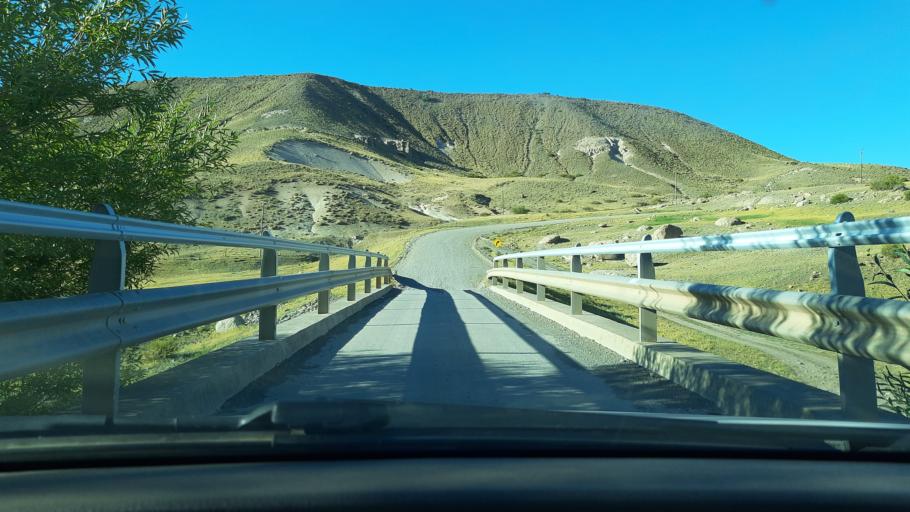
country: AR
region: Neuquen
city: Las Ovejas
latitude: -36.8233
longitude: -70.7073
